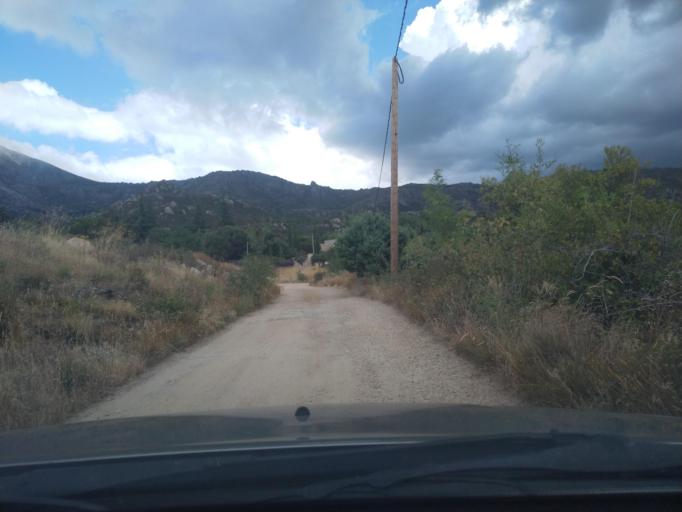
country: ES
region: Madrid
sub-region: Provincia de Madrid
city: Becerril de la Sierra
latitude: 40.7340
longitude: -3.9587
